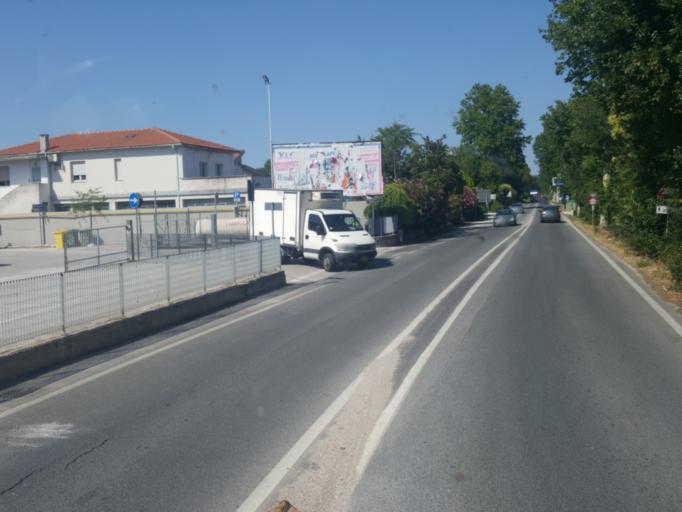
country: IT
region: The Marches
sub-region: Provincia di Ancona
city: Monsano
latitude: 43.5577
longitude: 13.2862
